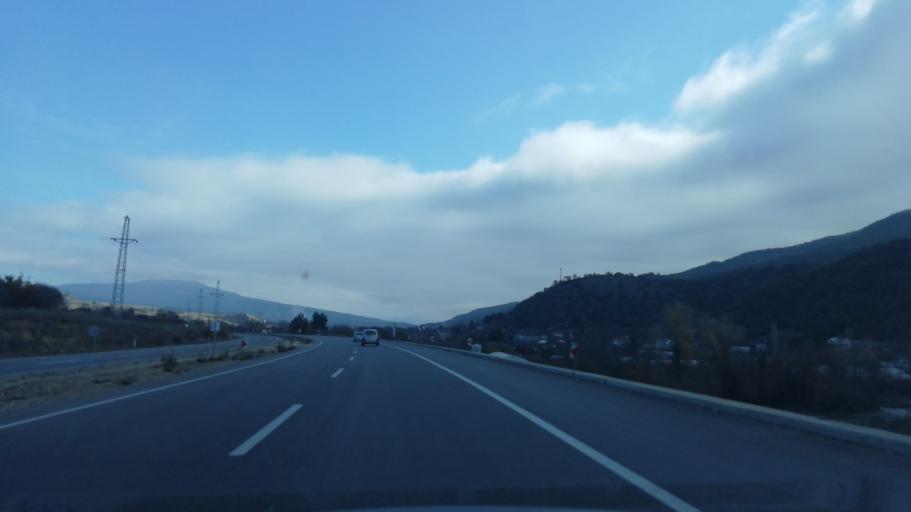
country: TR
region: Karabuk
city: Safranbolu
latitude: 41.2168
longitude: 32.7335
